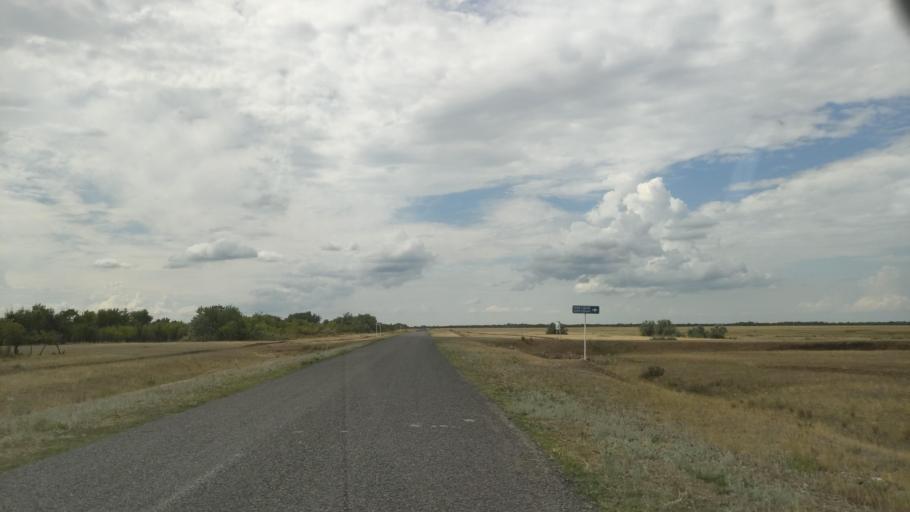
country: KZ
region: Pavlodar
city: Pavlodar
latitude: 52.6427
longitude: 77.0277
